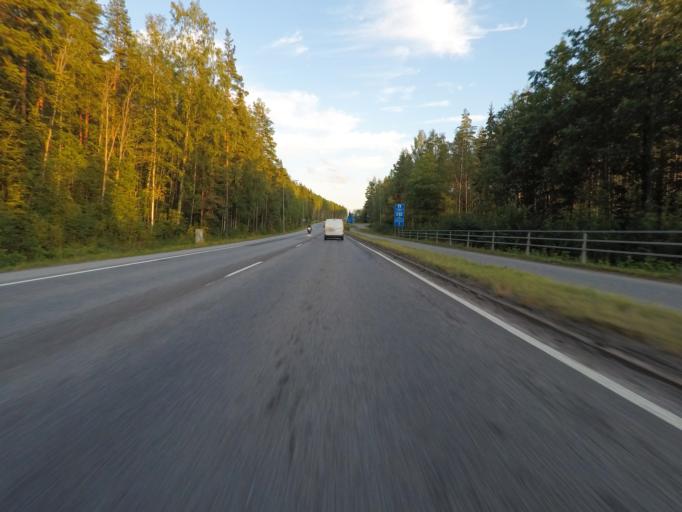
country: FI
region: Central Finland
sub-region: Jyvaeskylae
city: Saeynaetsalo
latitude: 62.2350
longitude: 25.8957
